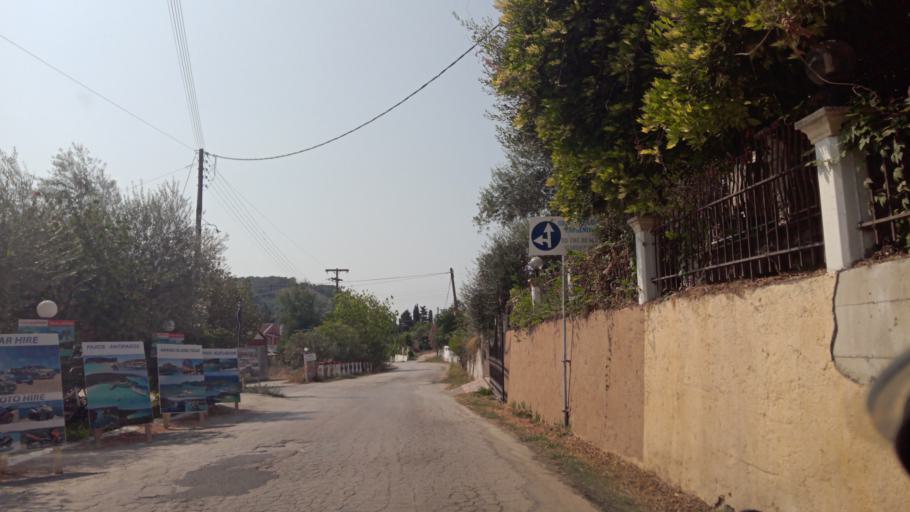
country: GR
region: Ionian Islands
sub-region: Nomos Kerkyras
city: Perivoli
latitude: 39.4043
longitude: 20.0274
